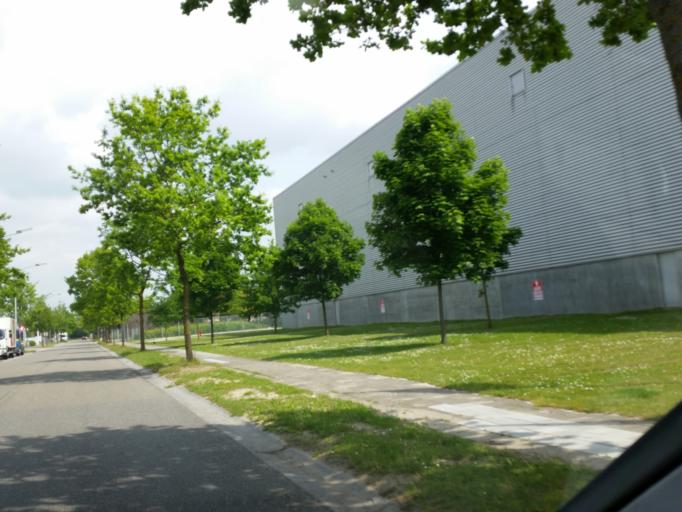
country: BE
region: Flanders
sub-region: Provincie Antwerpen
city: Mechelen
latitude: 51.0067
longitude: 4.4644
